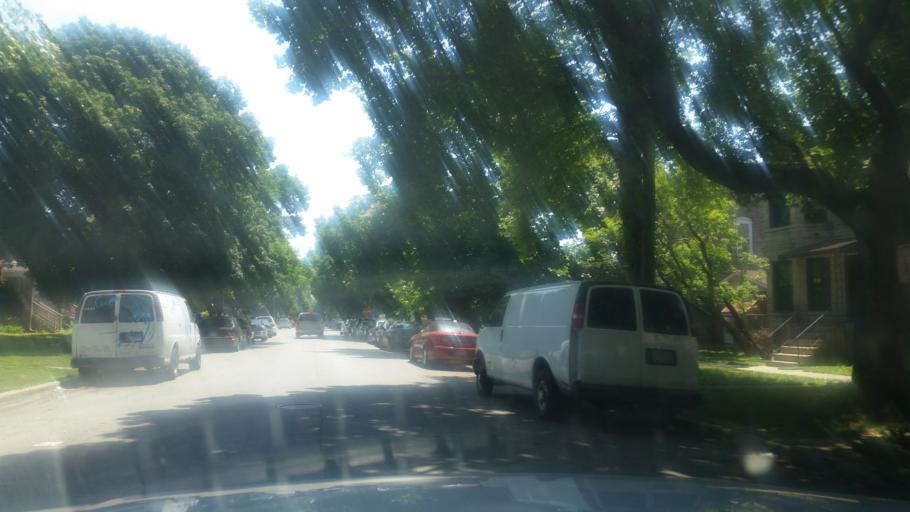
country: US
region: Illinois
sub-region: Cook County
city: Chicago
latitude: 41.7700
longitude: -87.6234
